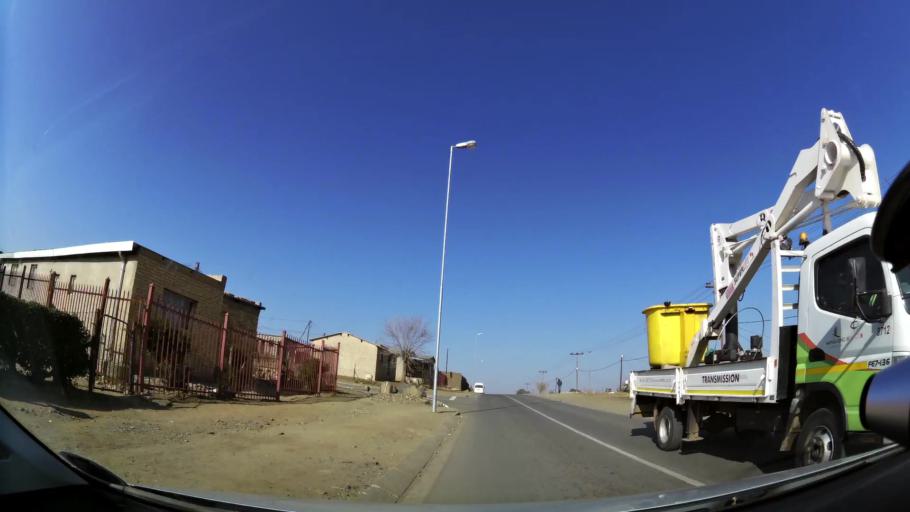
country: ZA
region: Orange Free State
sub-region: Mangaung Metropolitan Municipality
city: Bloemfontein
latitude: -29.1762
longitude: 26.2253
